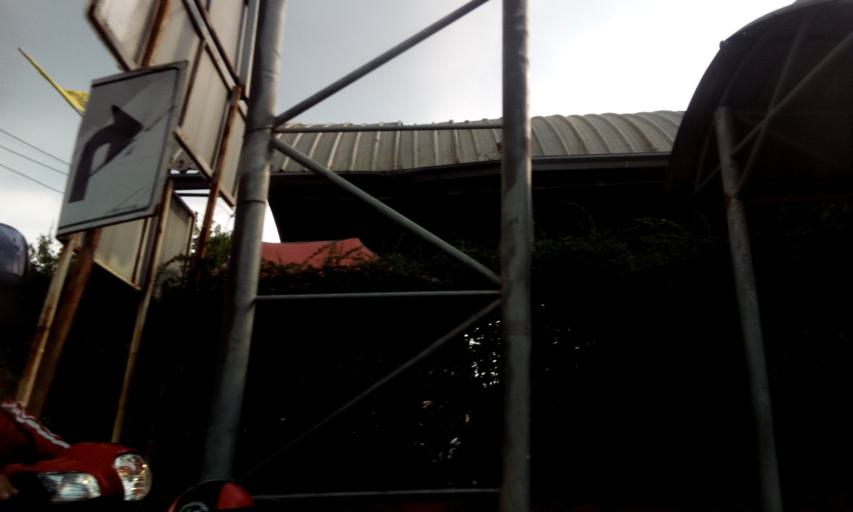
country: TH
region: Bangkok
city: Don Mueang
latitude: 13.9380
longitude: 100.5452
